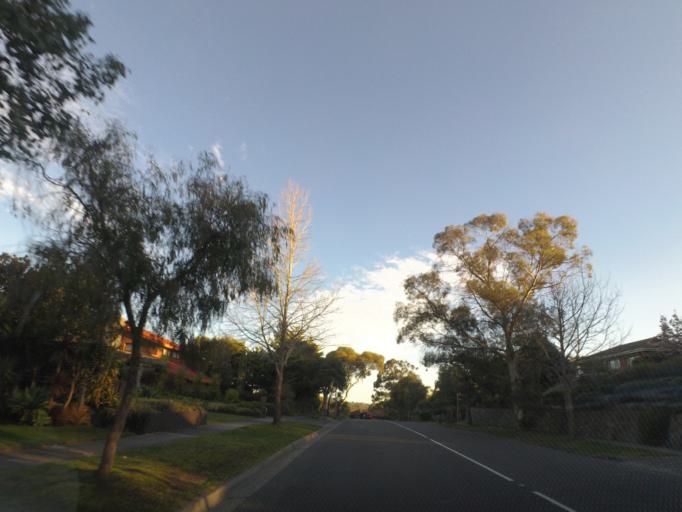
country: AU
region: Victoria
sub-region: Maroondah
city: Warranwood
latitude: -37.7871
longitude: 145.2530
